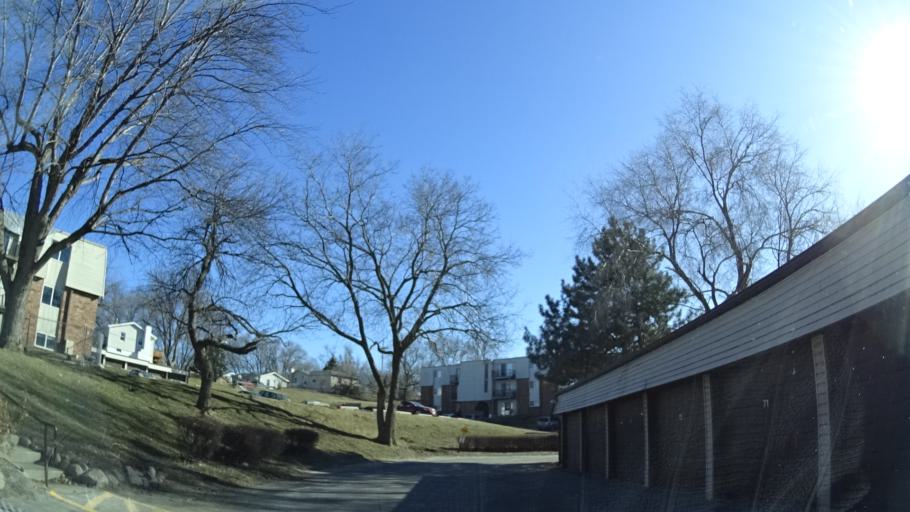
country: US
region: Nebraska
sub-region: Sarpy County
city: Bellevue
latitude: 41.1444
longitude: -95.9107
